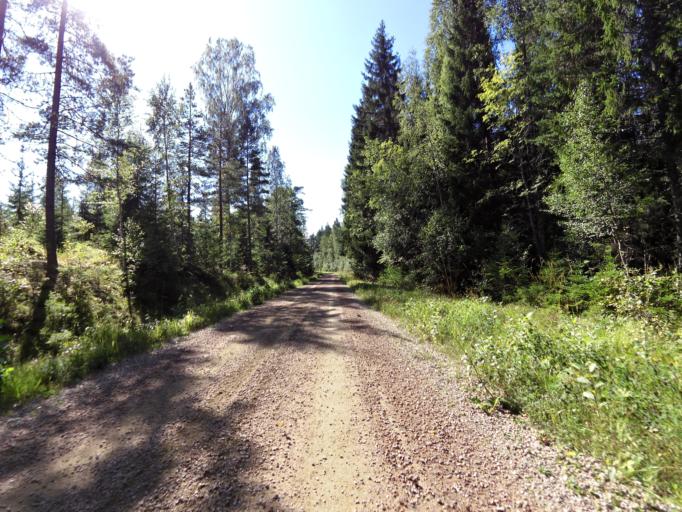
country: SE
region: Gaevleborg
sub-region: Ockelbo Kommun
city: Ockelbo
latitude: 60.8018
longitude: 16.8580
